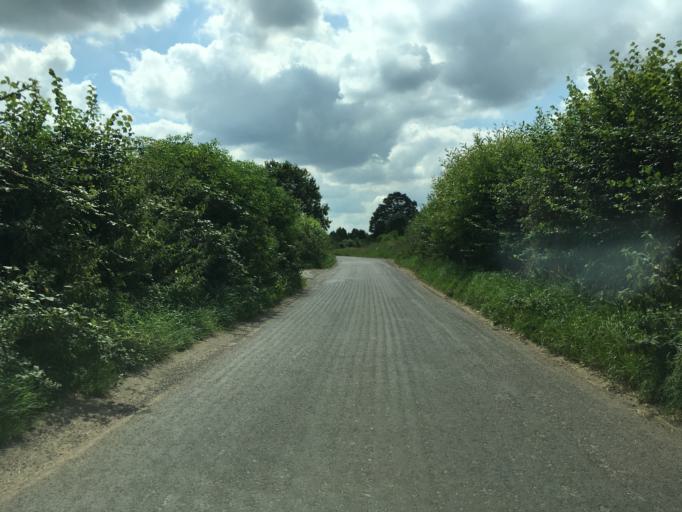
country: GB
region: England
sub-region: Gloucestershire
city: Gloucester
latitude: 51.9032
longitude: -2.2511
